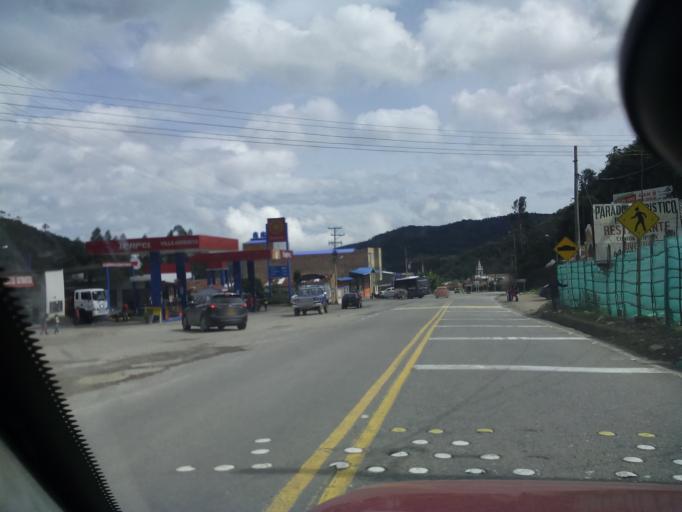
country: CO
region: Boyaca
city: Arcabuco
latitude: 5.7499
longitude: -73.4336
